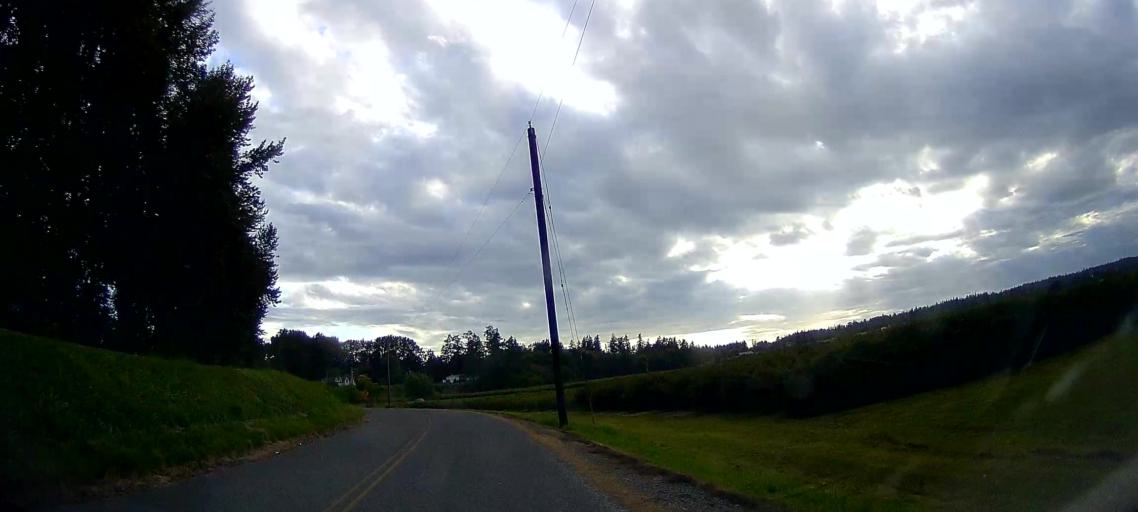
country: US
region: Washington
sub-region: Skagit County
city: Mount Vernon
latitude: 48.3671
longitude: -122.4136
